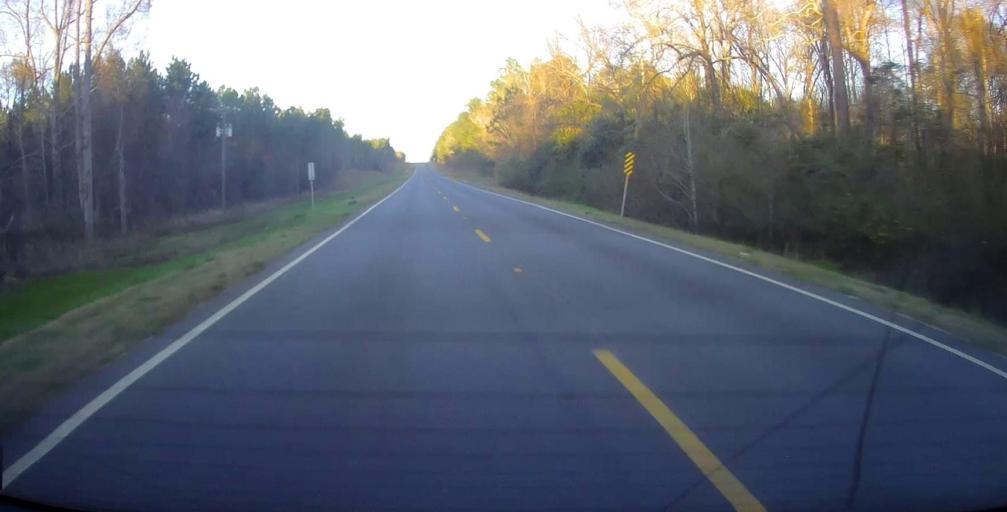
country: US
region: Georgia
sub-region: Laurens County
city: Dublin
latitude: 32.4178
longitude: -82.9520
